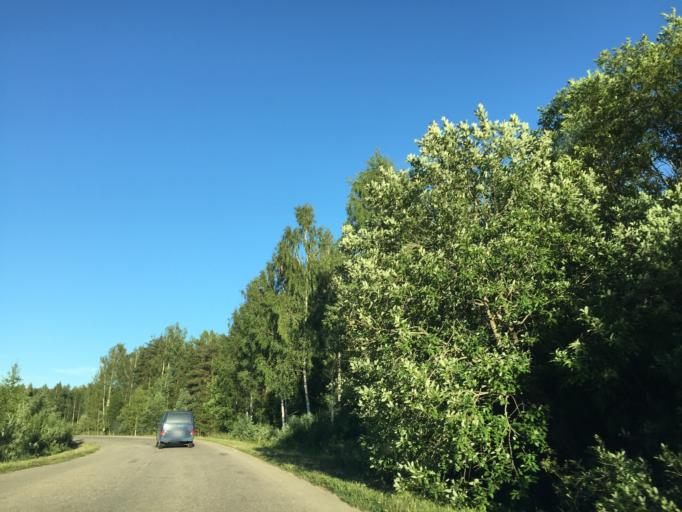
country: LV
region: Jekabpils Rajons
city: Jekabpils
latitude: 56.6086
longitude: 25.8381
